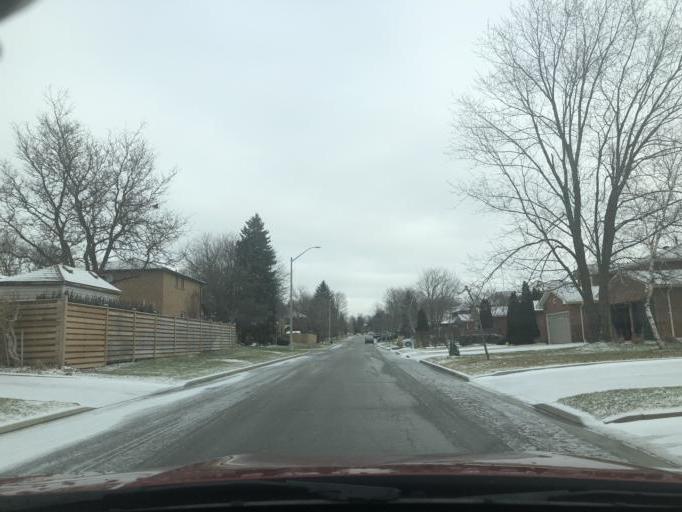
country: CA
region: Ontario
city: Markham
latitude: 43.8701
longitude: -79.2418
